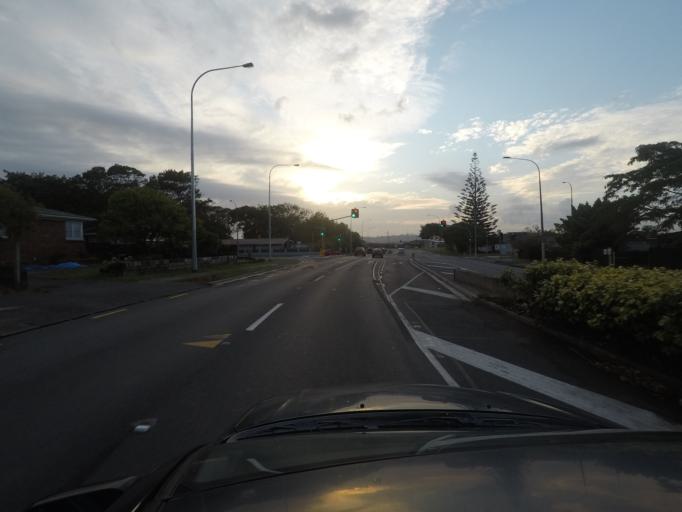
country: NZ
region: Auckland
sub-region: Auckland
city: Tamaki
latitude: -36.9235
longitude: 174.8844
